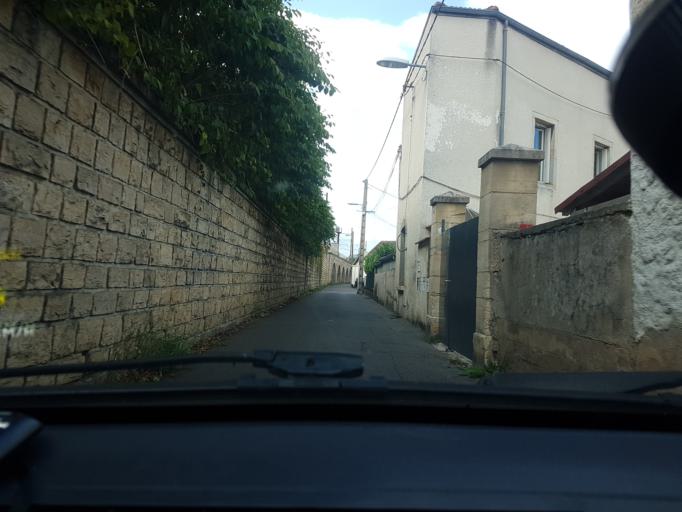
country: FR
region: Bourgogne
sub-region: Departement de la Cote-d'Or
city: Longvic
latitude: 47.3084
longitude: 5.0530
